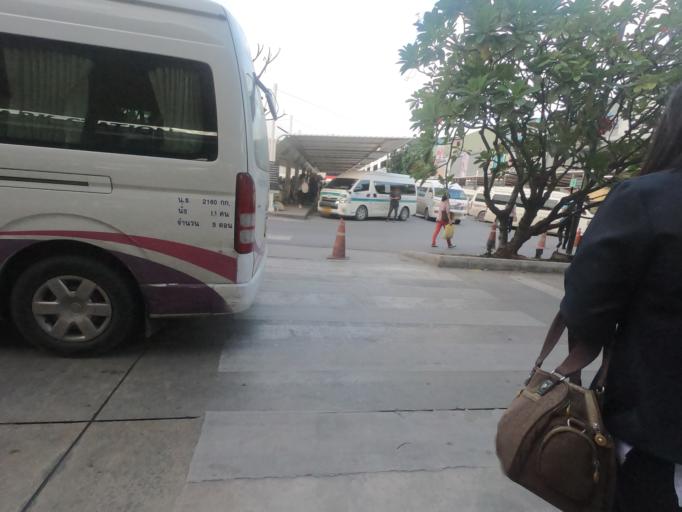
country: TH
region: Bangkok
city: Sai Mai
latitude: 13.9598
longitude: 100.6595
